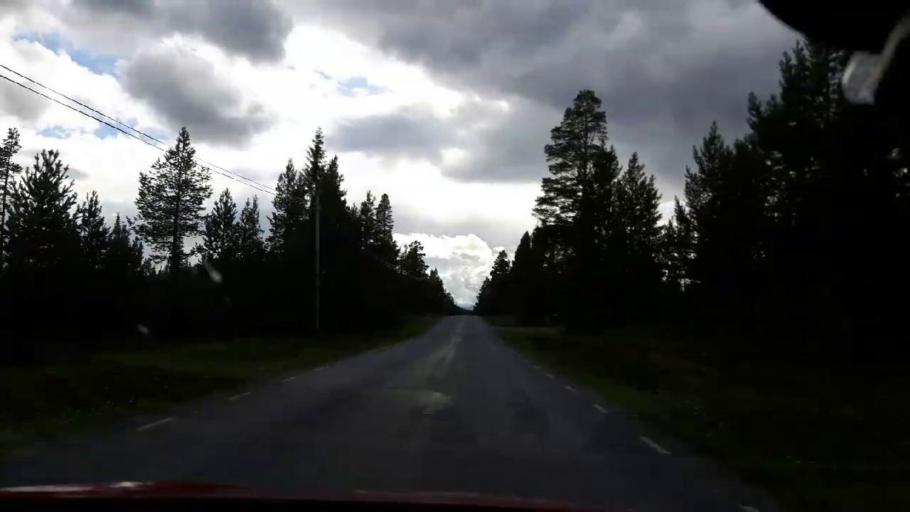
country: SE
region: Jaemtland
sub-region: Are Kommun
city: Are
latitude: 63.1755
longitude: 13.0974
